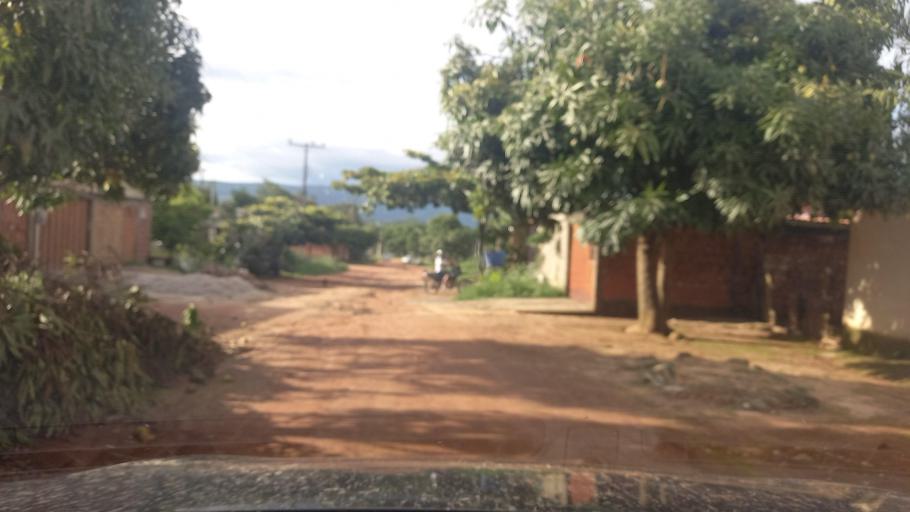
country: BR
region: Goias
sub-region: Cavalcante
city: Cavalcante
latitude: -13.7985
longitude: -47.4397
